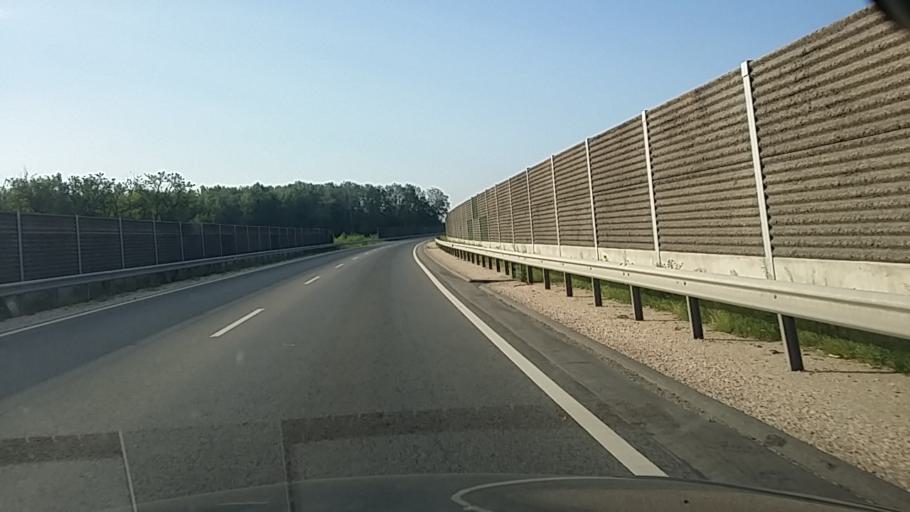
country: HU
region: Bacs-Kiskun
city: Kecskemet
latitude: 46.9380
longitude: 19.7117
